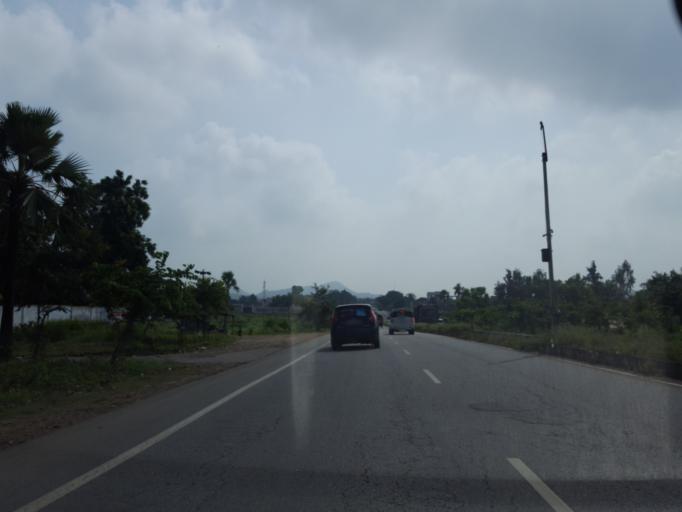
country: IN
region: Telangana
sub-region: Rangareddi
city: Ghatkesar
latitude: 17.2923
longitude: 78.7558
